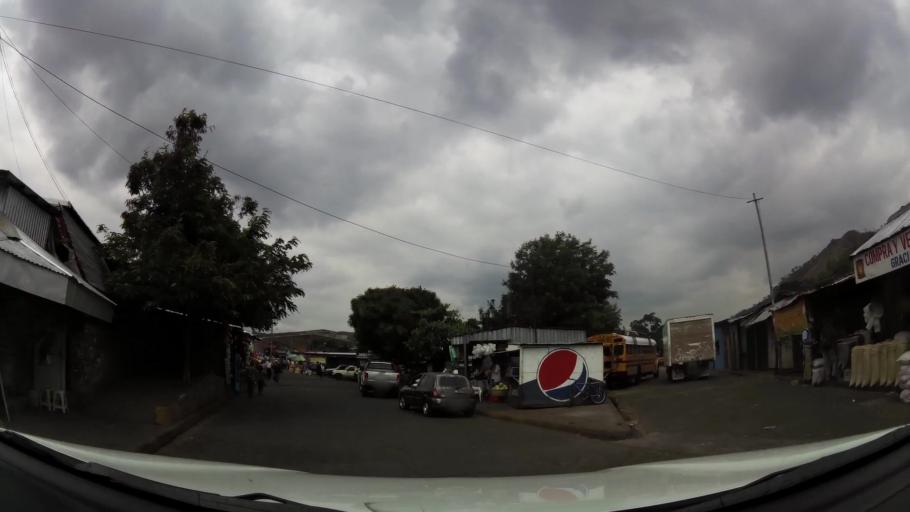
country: NI
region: Matagalpa
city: Matagalpa
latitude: 12.9217
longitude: -85.9248
